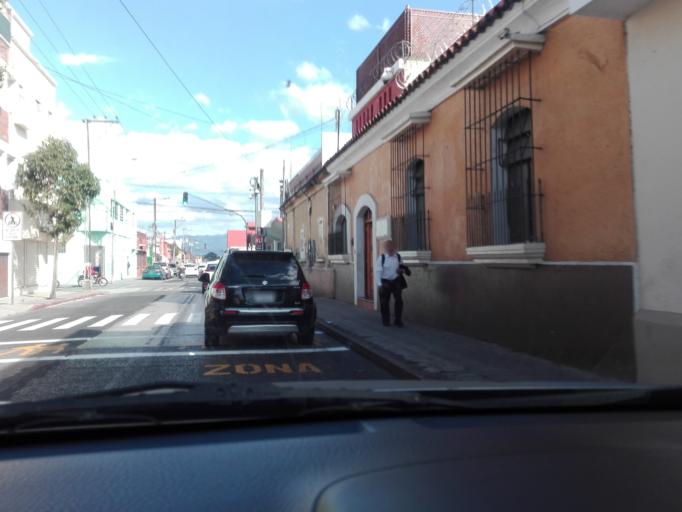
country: GT
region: Guatemala
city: Guatemala City
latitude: 14.6455
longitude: -90.5115
